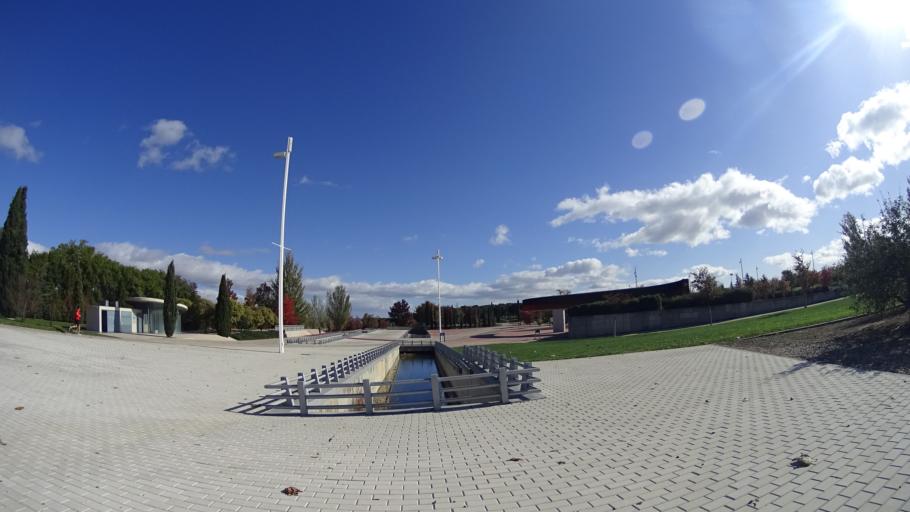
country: ES
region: Madrid
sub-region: Provincia de Madrid
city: San Blas
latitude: 40.4637
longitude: -3.6104
